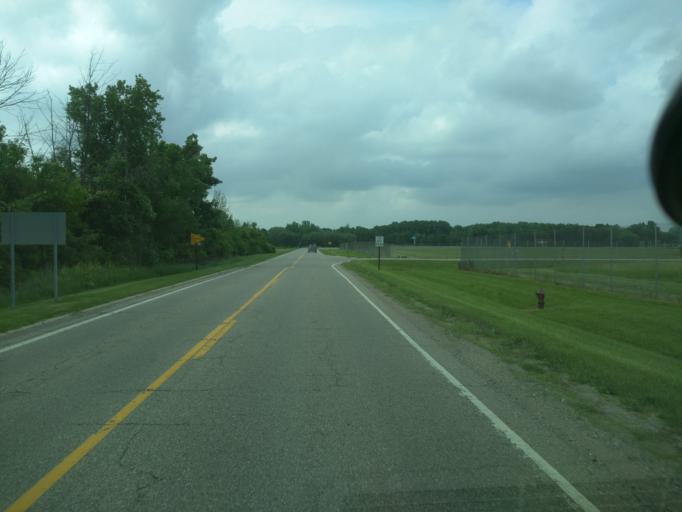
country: US
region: Michigan
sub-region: Ingham County
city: Edgemont Park
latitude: 42.7753
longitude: -84.6074
